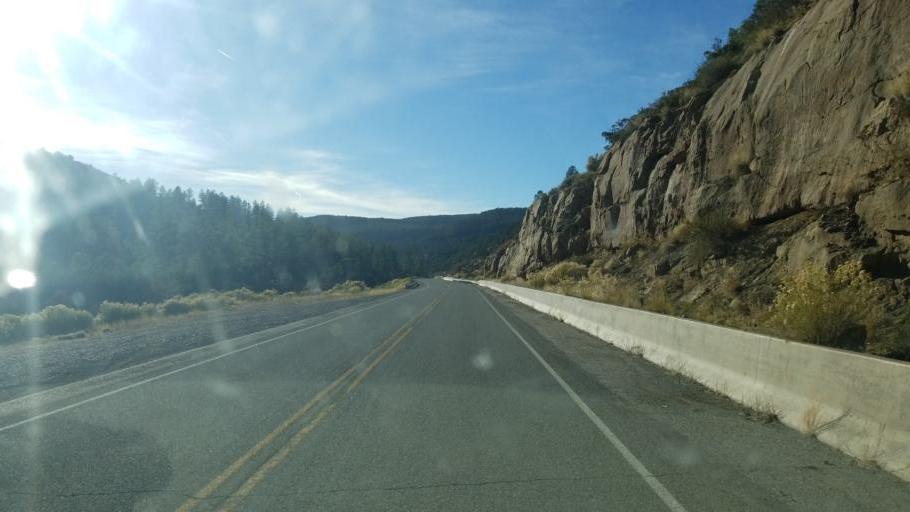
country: US
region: New Mexico
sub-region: Rio Arriba County
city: Navajo
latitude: 36.7358
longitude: -107.2512
